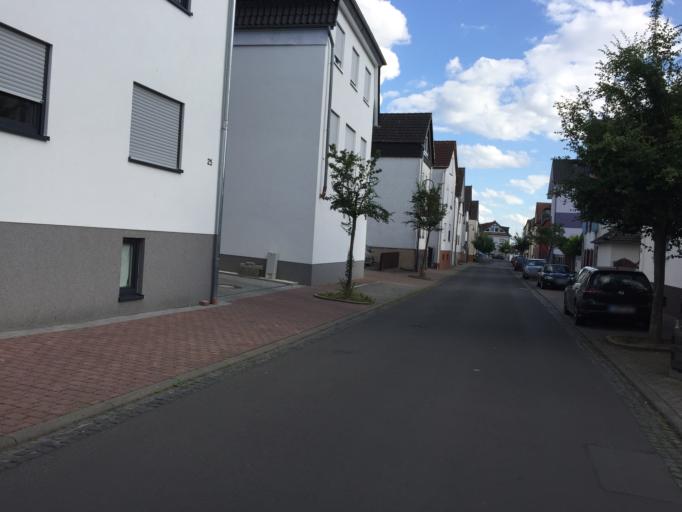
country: DE
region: Hesse
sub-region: Regierungsbezirk Darmstadt
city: Karben
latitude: 50.2259
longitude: 8.7738
